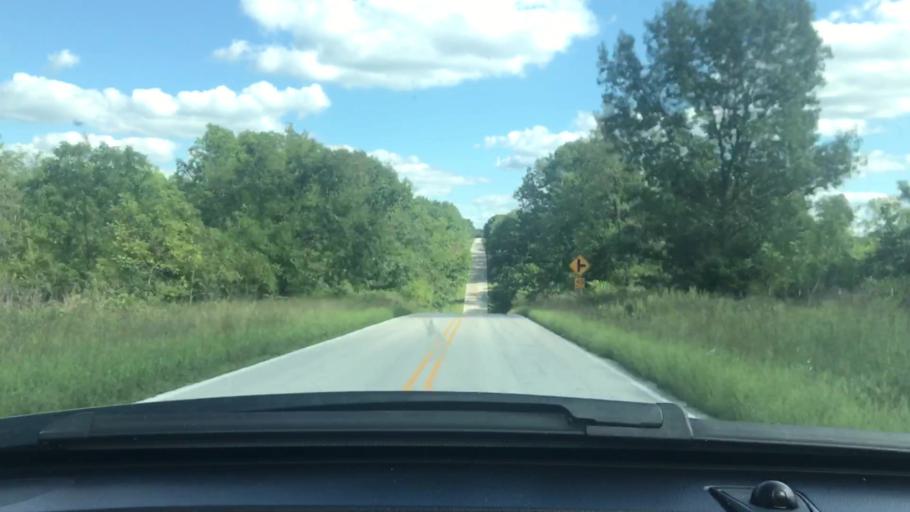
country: US
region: Missouri
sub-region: Wright County
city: Hartville
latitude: 37.3860
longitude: -92.4431
